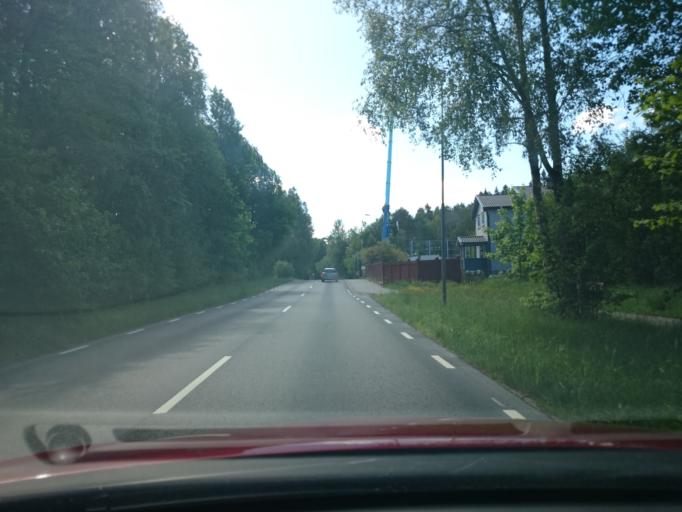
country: SE
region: Vaestra Goetaland
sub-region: Harryda Kommun
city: Landvetter
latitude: 57.6933
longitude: 12.2064
